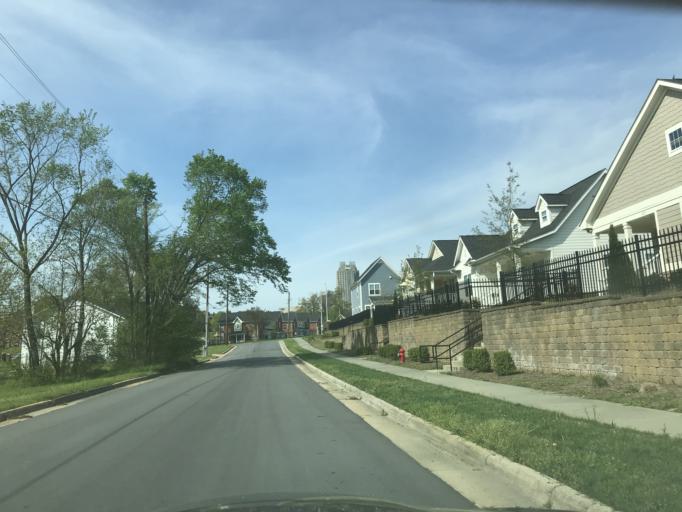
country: US
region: North Carolina
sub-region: Wake County
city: Raleigh
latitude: 35.7649
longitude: -78.6422
